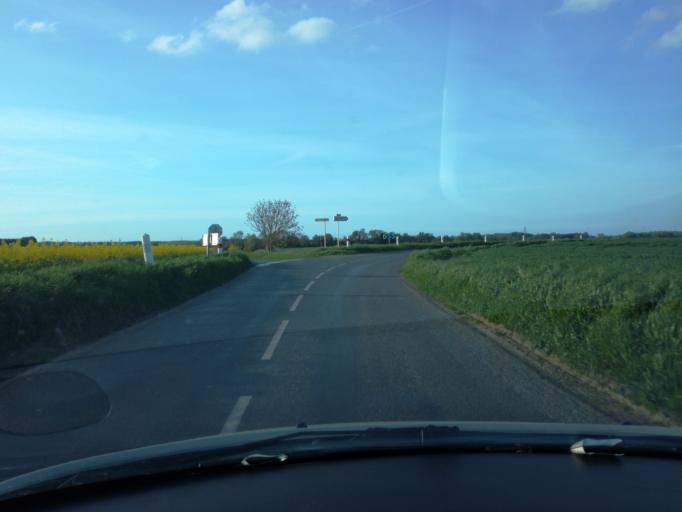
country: FR
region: Picardie
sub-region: Departement de la Somme
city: Poix-de-Picardie
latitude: 49.7985
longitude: 1.9941
